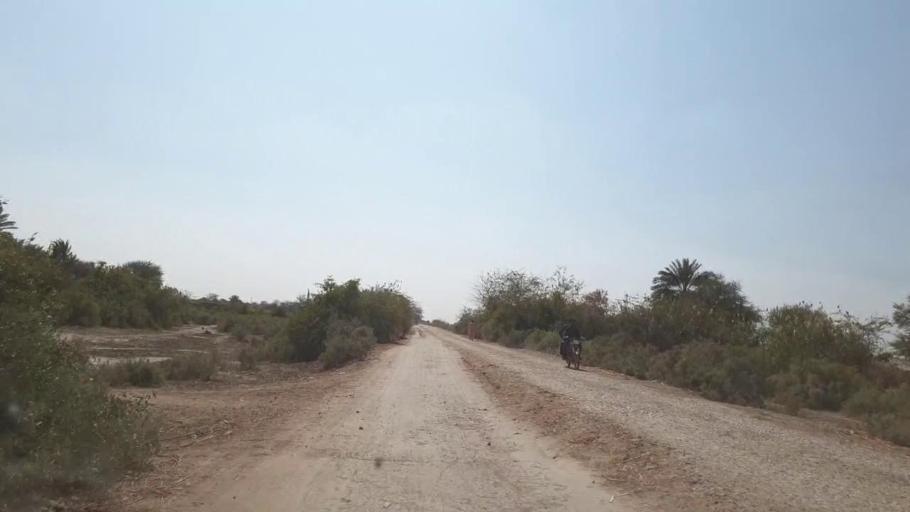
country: PK
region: Sindh
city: Mirpur Khas
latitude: 25.7303
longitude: 69.0722
